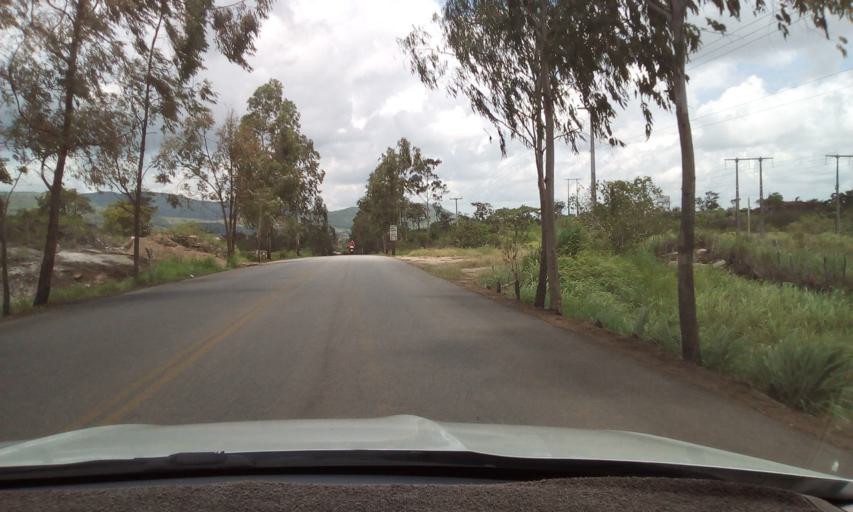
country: BR
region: Pernambuco
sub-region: Bonito
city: Bonito
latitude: -8.4530
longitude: -35.7294
